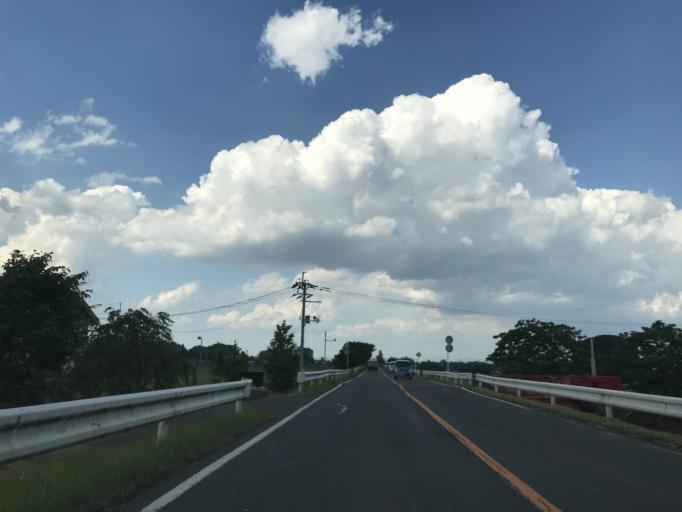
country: JP
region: Miyagi
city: Wakuya
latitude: 38.5908
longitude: 141.1630
